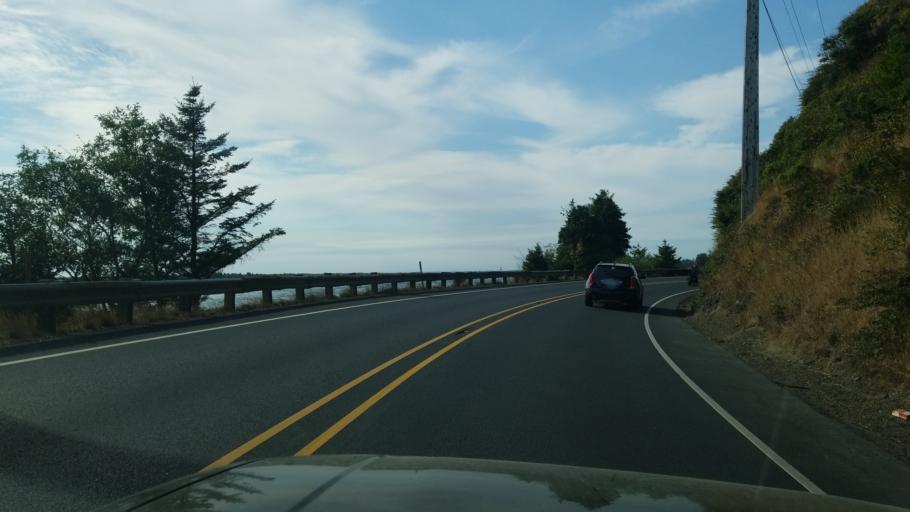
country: US
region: Oregon
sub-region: Tillamook County
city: Rockaway Beach
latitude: 45.5606
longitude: -123.9334
